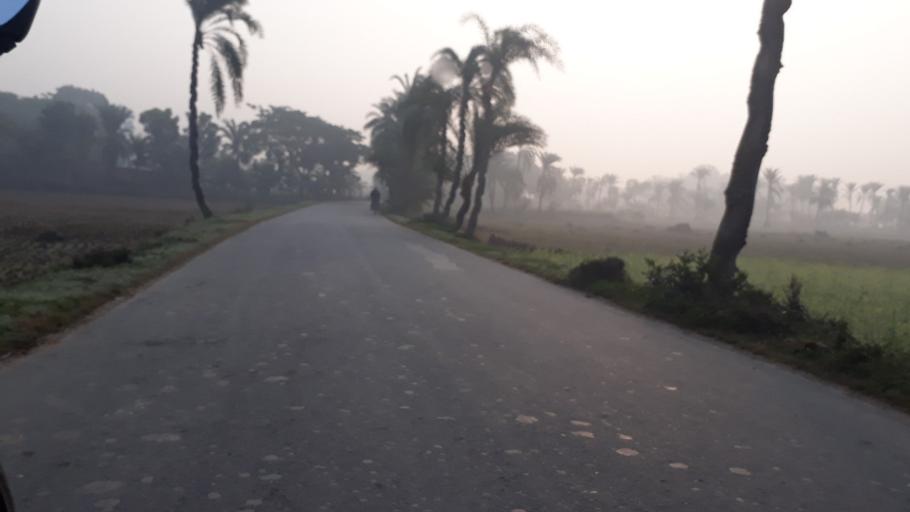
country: BD
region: Khulna
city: Jhingergacha
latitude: 23.2778
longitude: 88.9550
